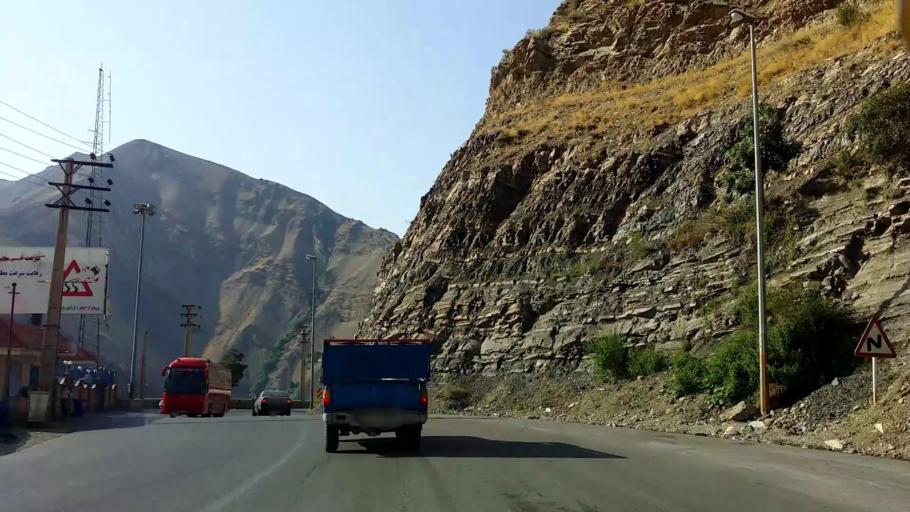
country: IR
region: Alborz
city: Karaj
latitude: 35.9561
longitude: 51.0853
